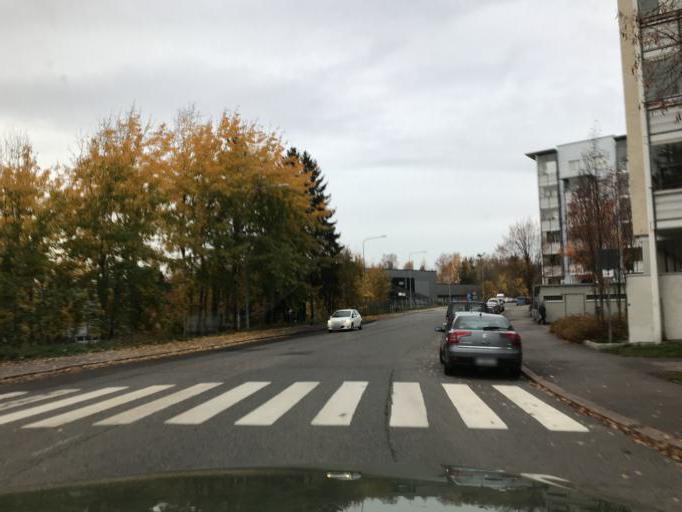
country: FI
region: Uusimaa
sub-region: Helsinki
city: Vantaa
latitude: 60.2542
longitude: 25.0702
